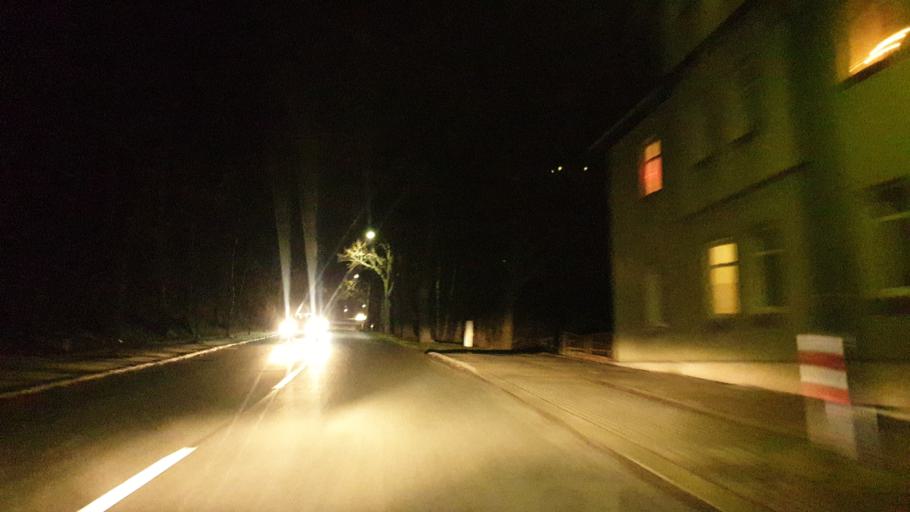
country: DE
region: Saxony
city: Oelsnitz
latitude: 50.7237
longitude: 12.7136
